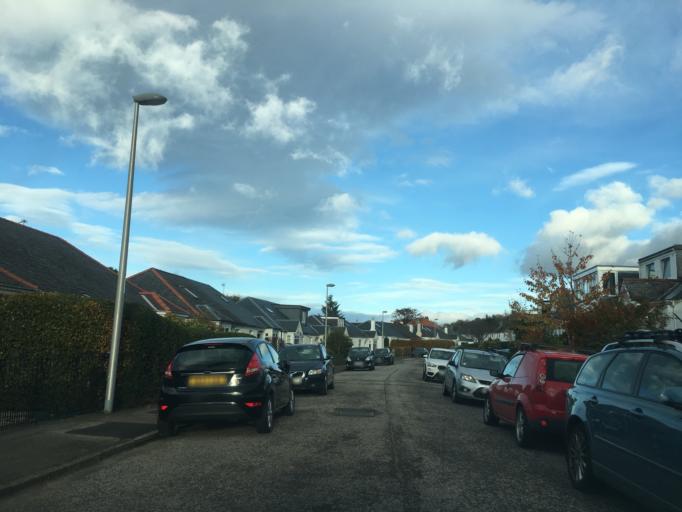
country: GB
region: Scotland
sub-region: Edinburgh
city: Colinton
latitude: 55.9190
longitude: -3.2449
